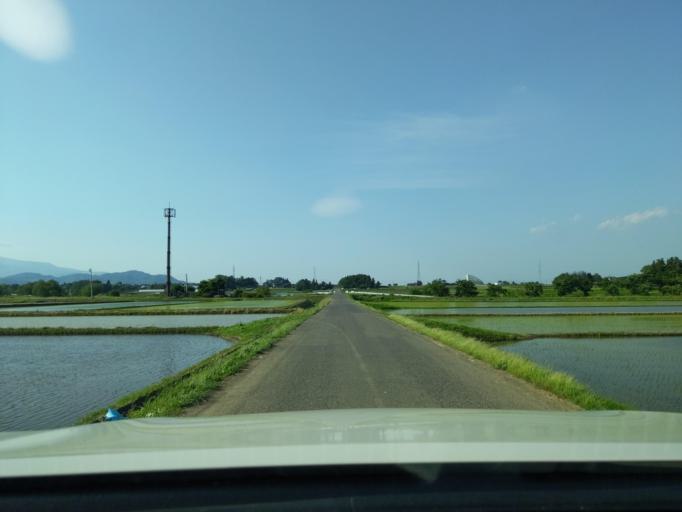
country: JP
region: Fukushima
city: Koriyama
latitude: 37.4460
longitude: 140.3645
